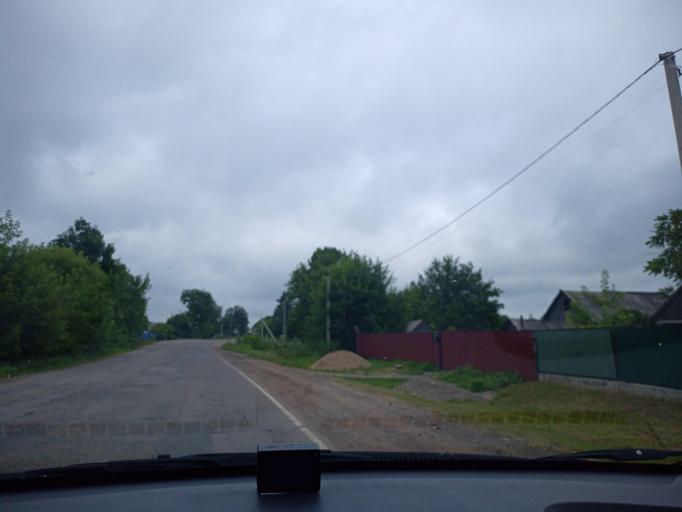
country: RU
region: Primorskiy
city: Novopokrovka
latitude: 45.8945
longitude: 134.8629
